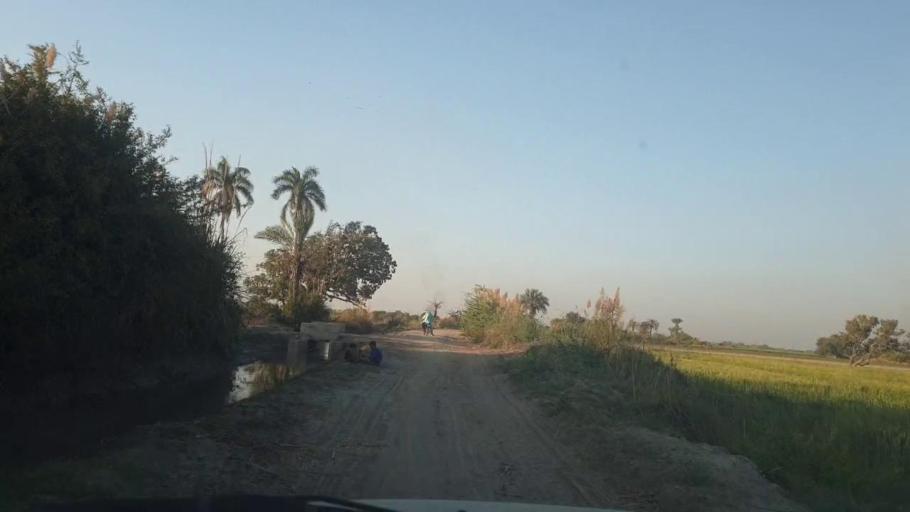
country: PK
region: Sindh
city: Mirpur Khas
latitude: 25.4720
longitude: 69.0865
